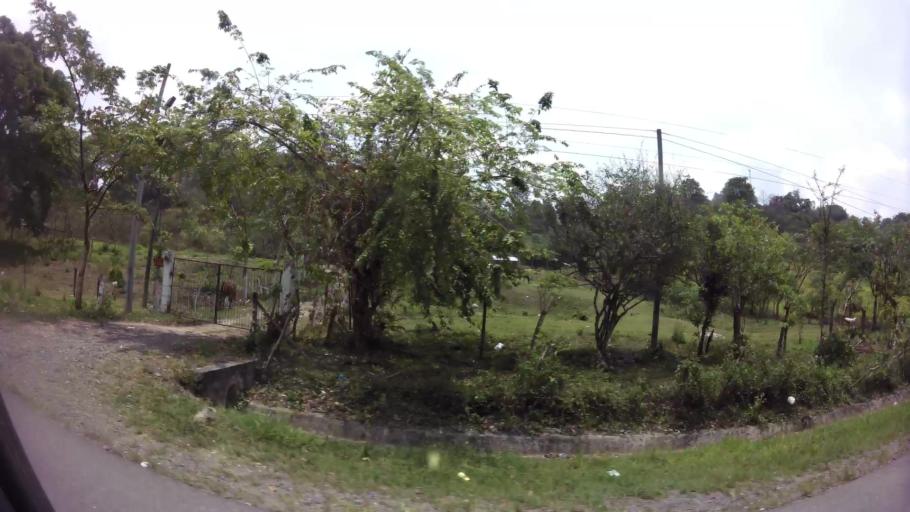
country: HN
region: Comayagua
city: Taulabe
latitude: 14.6801
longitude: -87.9564
